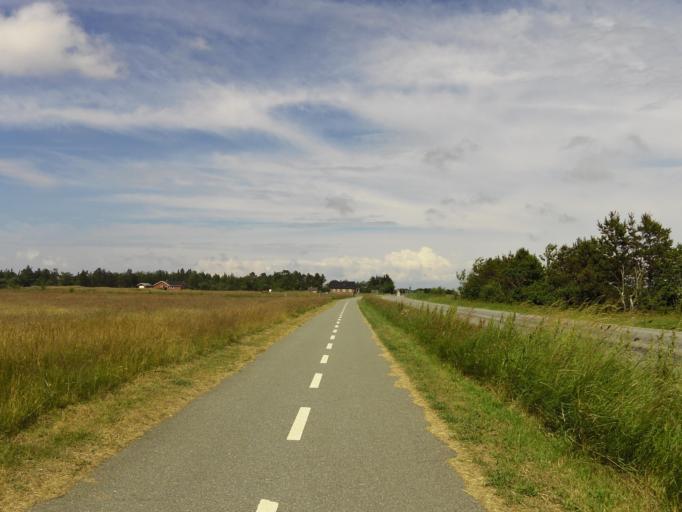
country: DE
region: Schleswig-Holstein
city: List
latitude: 55.1590
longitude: 8.5516
